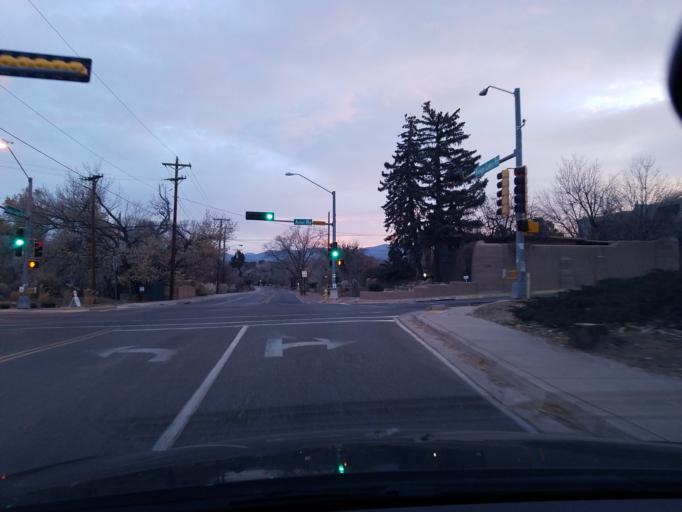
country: US
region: New Mexico
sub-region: Santa Fe County
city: Santa Fe
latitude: 35.6933
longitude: -105.9346
